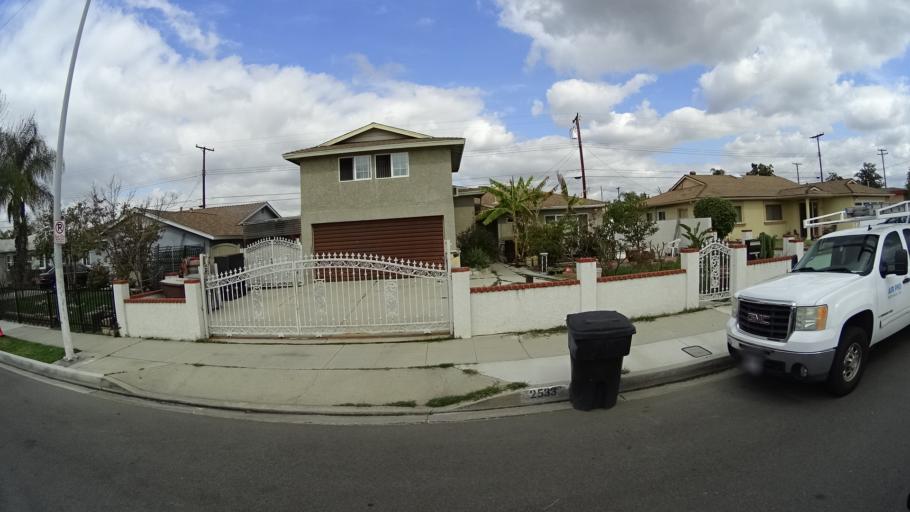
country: US
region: California
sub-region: Orange County
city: Buena Park
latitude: 33.8425
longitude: -117.9734
